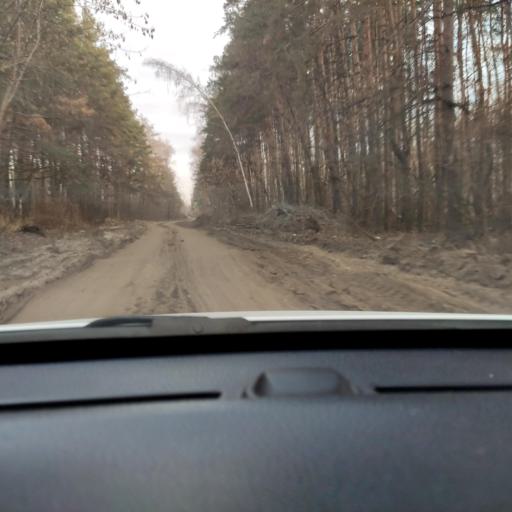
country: RU
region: Voronezj
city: Somovo
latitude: 51.6969
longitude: 39.2807
